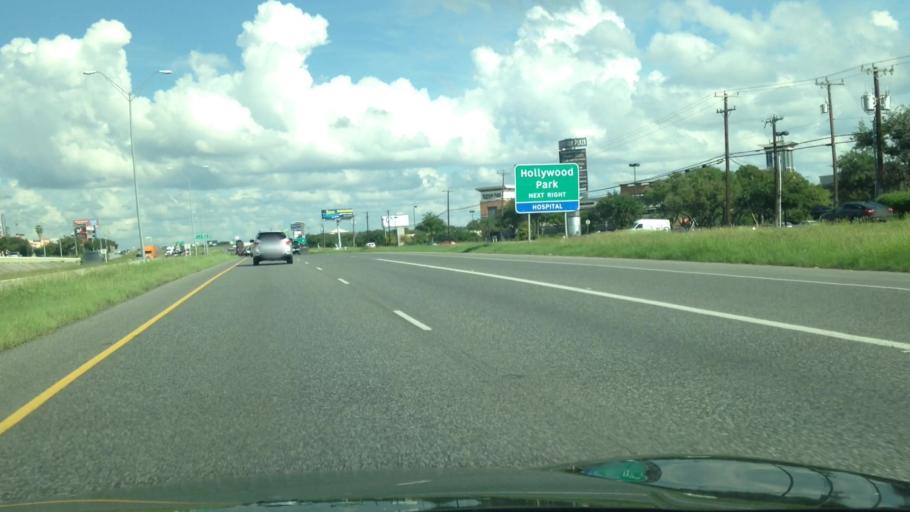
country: US
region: Texas
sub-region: Bexar County
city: Hollywood Park
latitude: 29.6081
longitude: -98.5034
